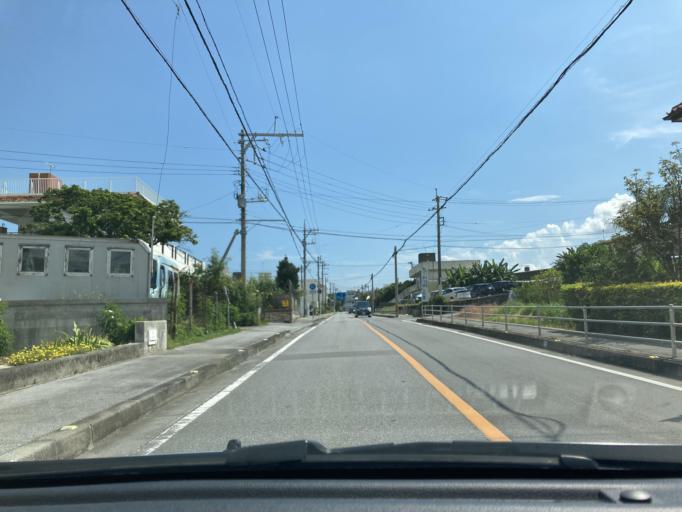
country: JP
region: Okinawa
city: Tomigusuku
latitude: 26.1793
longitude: 127.7201
